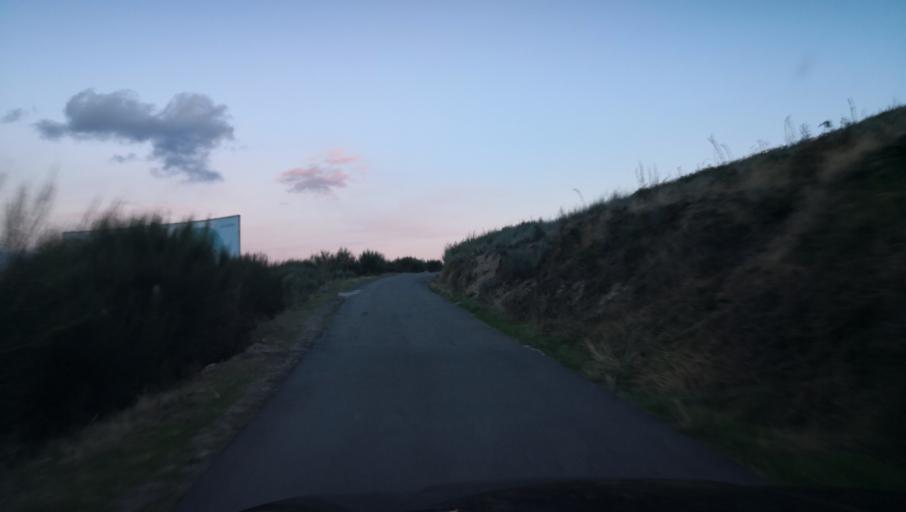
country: PT
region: Vila Real
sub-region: Santa Marta de Penaguiao
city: Santa Marta de Penaguiao
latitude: 41.2640
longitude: -7.7951
